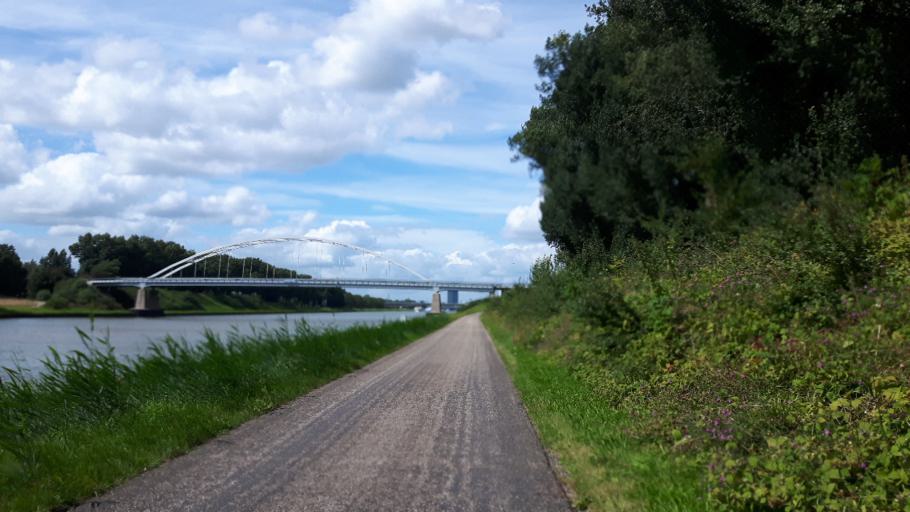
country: NL
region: Utrecht
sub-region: Gemeente Nieuwegein
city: Nieuwegein
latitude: 52.0324
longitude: 5.1144
